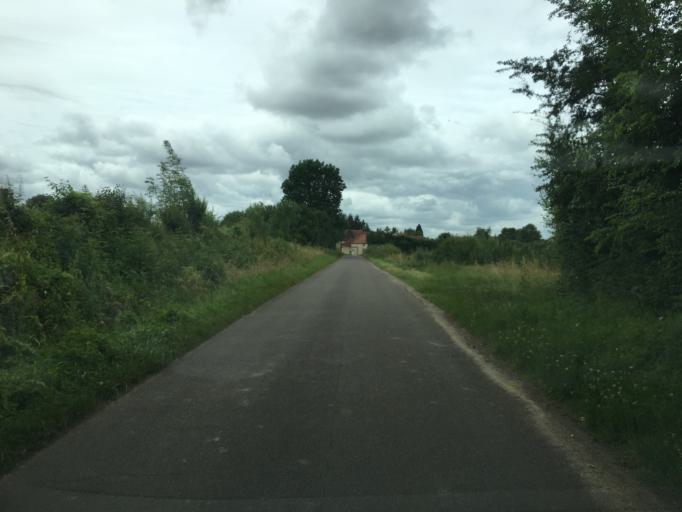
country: FR
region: Bourgogne
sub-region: Departement de l'Yonne
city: Fleury-la-Vallee
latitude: 47.8636
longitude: 3.4126
